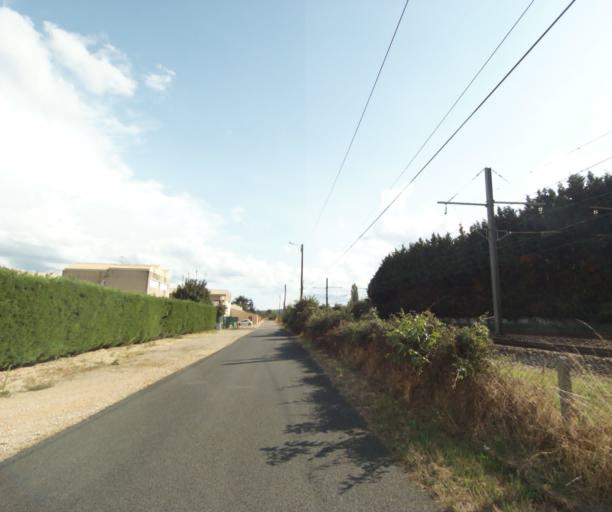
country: FR
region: Bourgogne
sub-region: Departement de Saone-et-Loire
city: Tournus
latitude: 46.5759
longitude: 4.9054
